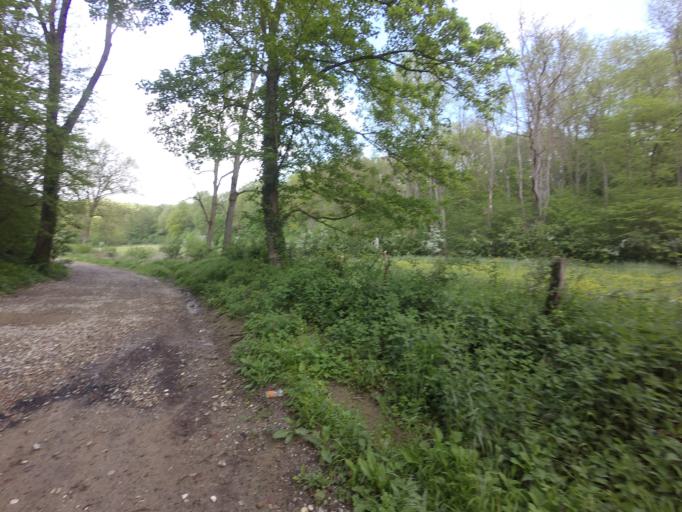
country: NL
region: Limburg
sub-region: Gemeente Maastricht
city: Heer
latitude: 50.8222
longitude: 5.7655
